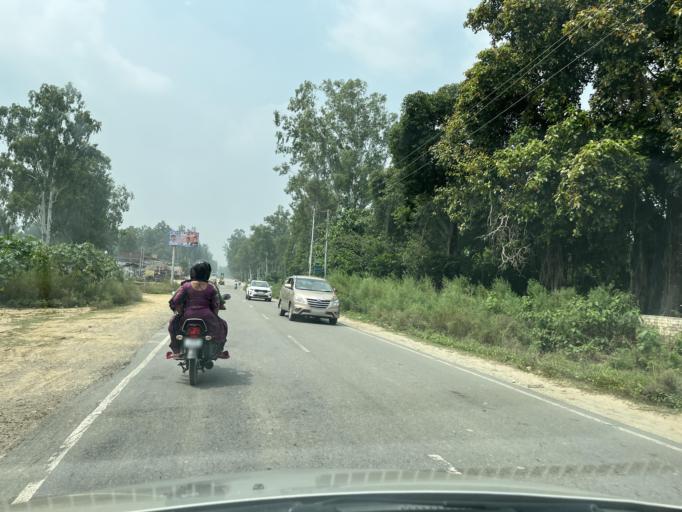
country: IN
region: Uttarakhand
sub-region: Haridwar
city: Sultanpur
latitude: 29.7486
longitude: 78.2613
